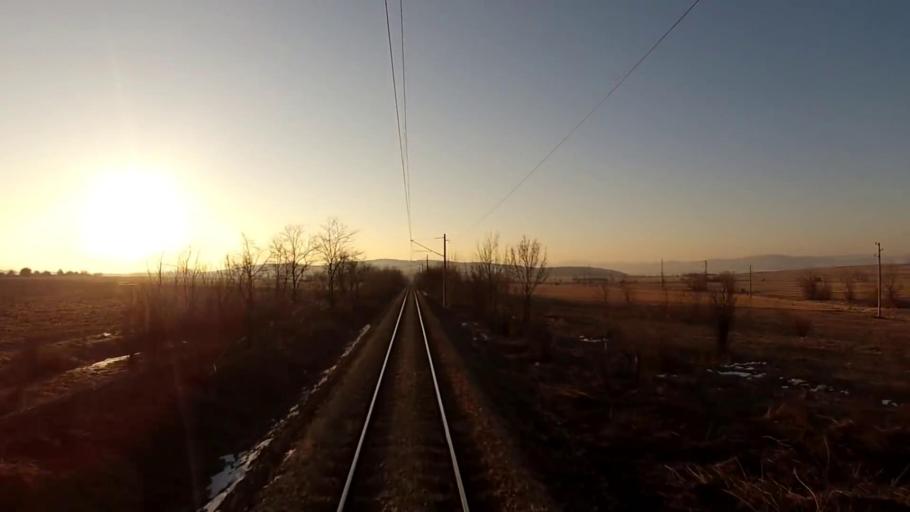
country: BG
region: Sofiya
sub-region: Obshtina Slivnitsa
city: Slivnitsa
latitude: 42.8796
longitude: 22.9879
